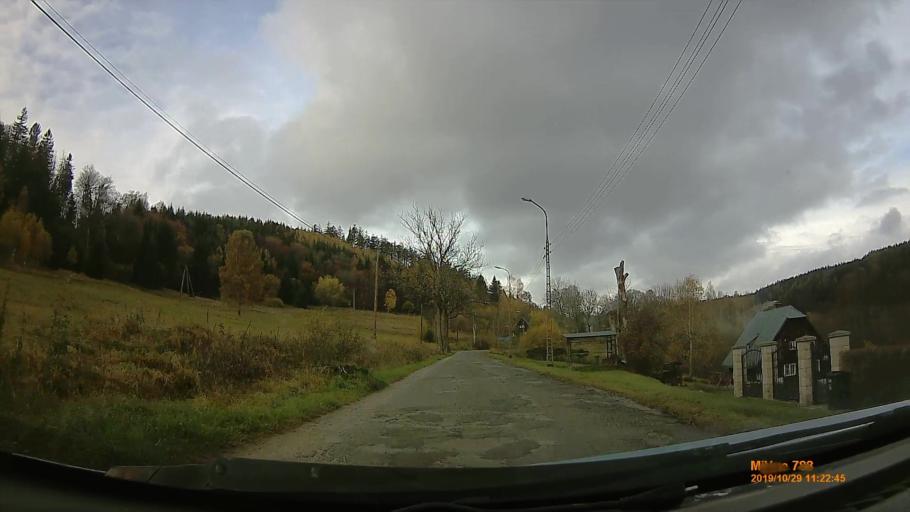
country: PL
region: Lower Silesian Voivodeship
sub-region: Powiat klodzki
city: Szczytna
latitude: 50.4352
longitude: 16.4295
